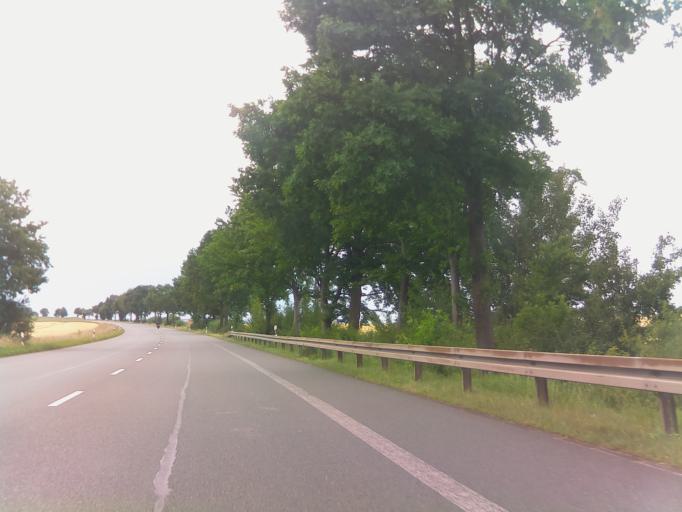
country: DE
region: North Rhine-Westphalia
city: Warburg
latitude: 51.5224
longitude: 9.1435
